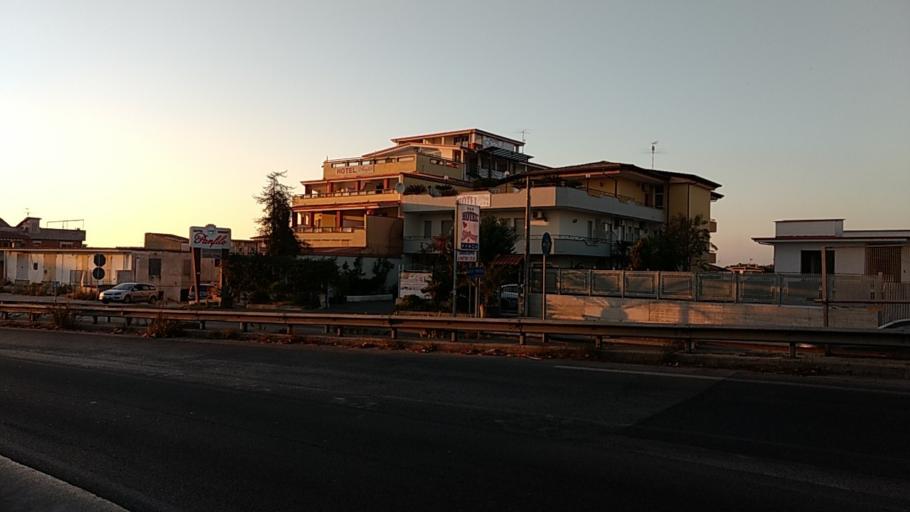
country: IT
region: Campania
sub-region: Provincia di Napoli
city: Masseria Vecchia Ovest
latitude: 40.9343
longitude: 14.0478
